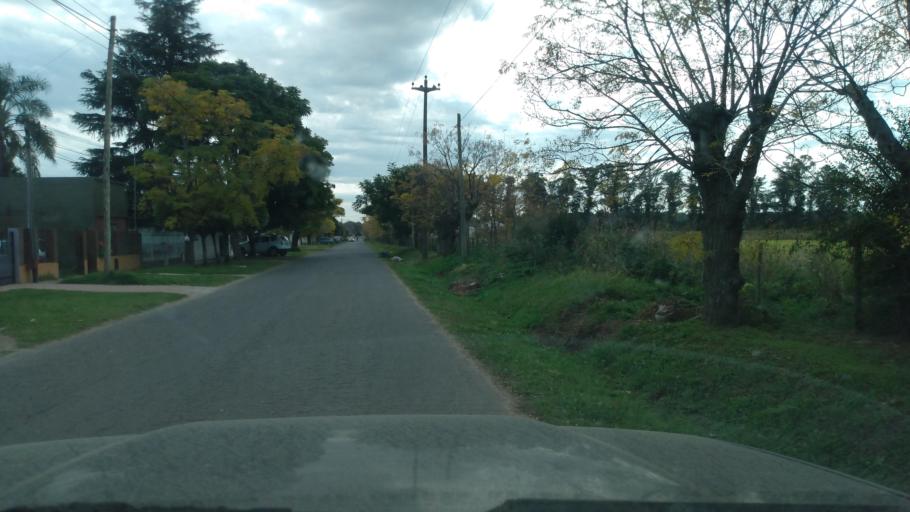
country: AR
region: Buenos Aires
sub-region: Partido de Lujan
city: Lujan
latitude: -34.5981
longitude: -59.1738
